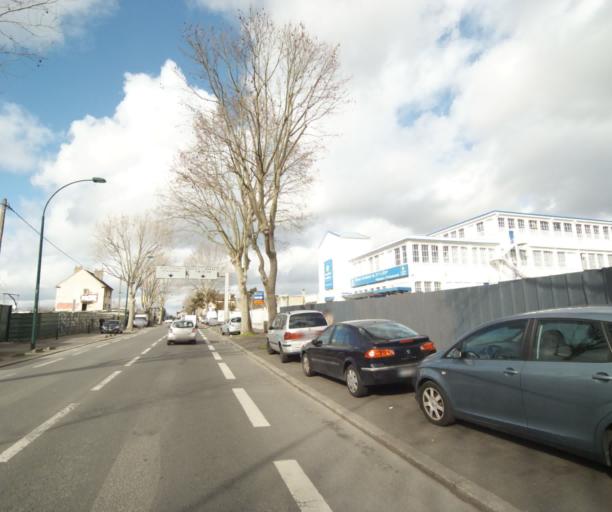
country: FR
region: Ile-de-France
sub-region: Departement de Seine-Saint-Denis
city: Villetaneuse
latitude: 48.9568
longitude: 2.3316
